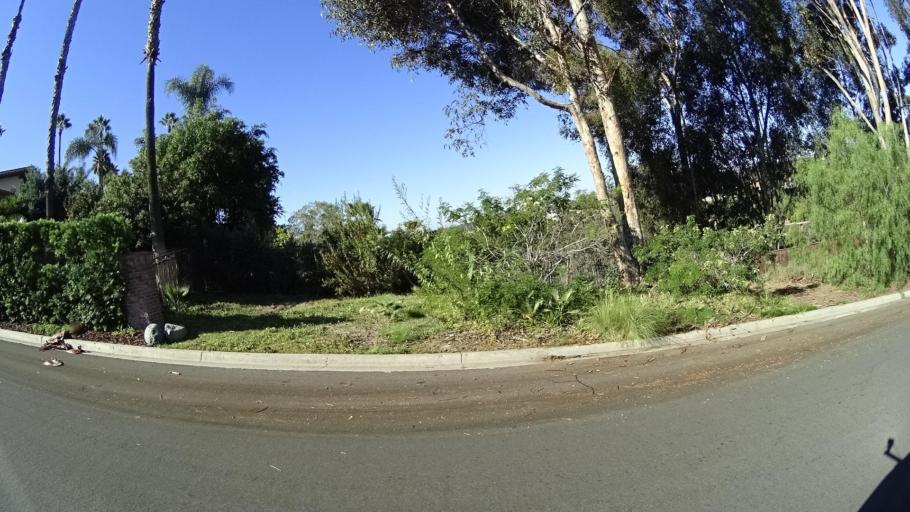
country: US
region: California
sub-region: San Diego County
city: Bonita
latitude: 32.6747
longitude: -117.0078
